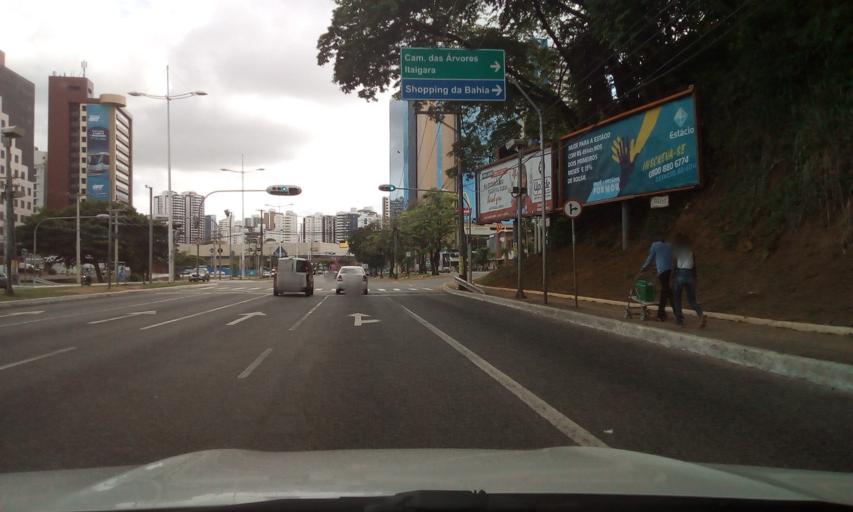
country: BR
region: Bahia
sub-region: Salvador
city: Salvador
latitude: -12.9889
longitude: -38.4696
